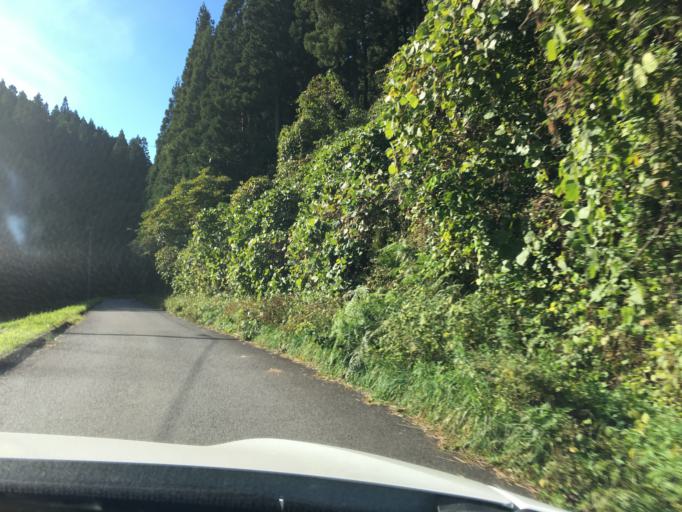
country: JP
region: Fukushima
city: Ishikawa
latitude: 37.1322
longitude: 140.5498
